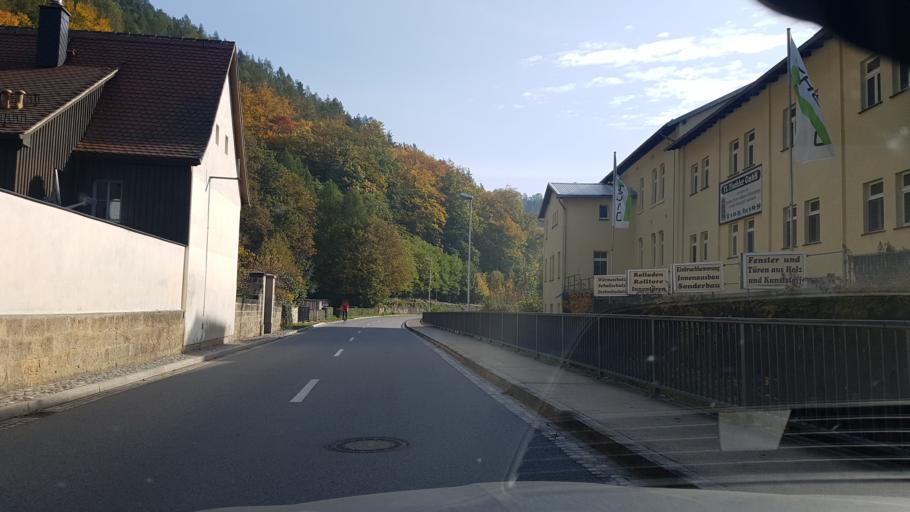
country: DE
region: Saxony
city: Konigstein
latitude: 50.9142
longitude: 14.0630
